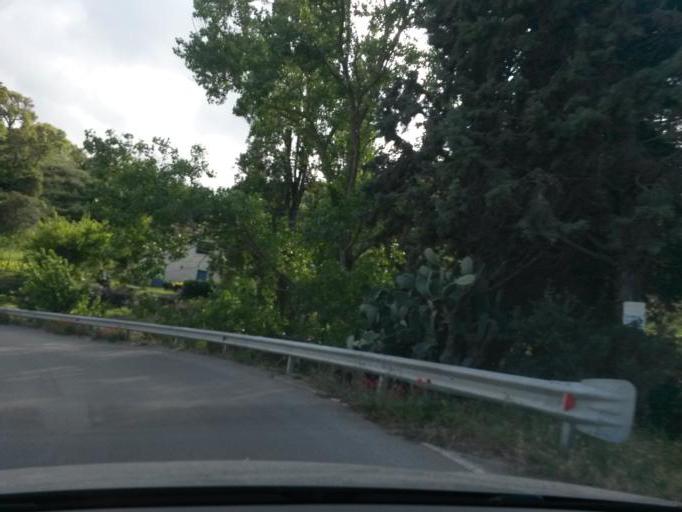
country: IT
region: Tuscany
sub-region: Provincia di Livorno
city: Rio nell'Elba
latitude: 42.8035
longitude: 10.4021
